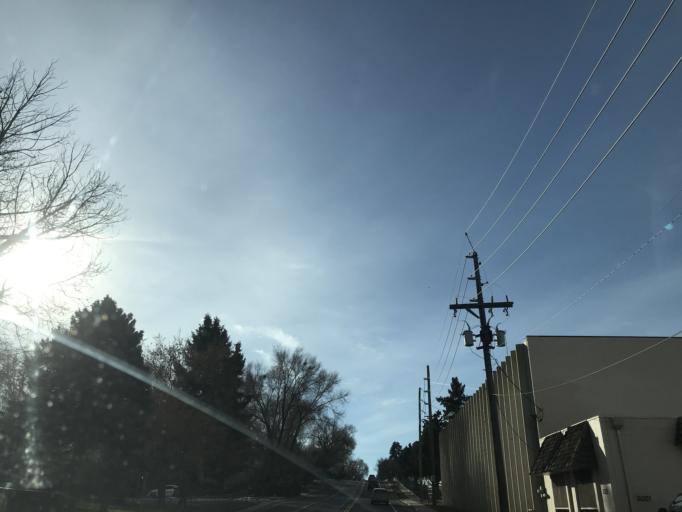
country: US
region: Colorado
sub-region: Arapahoe County
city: Littleton
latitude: 39.6075
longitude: -105.0163
